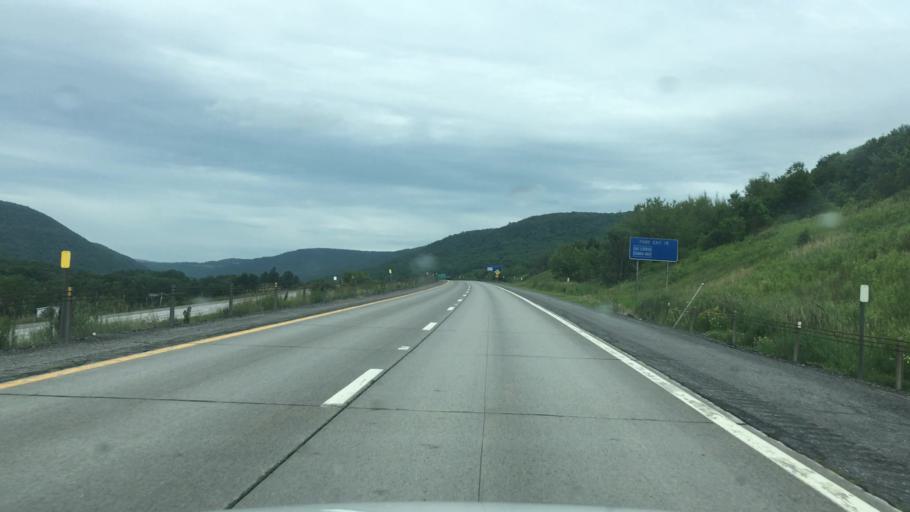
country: US
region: New York
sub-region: Otsego County
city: Worcester
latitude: 42.5393
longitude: -74.8281
